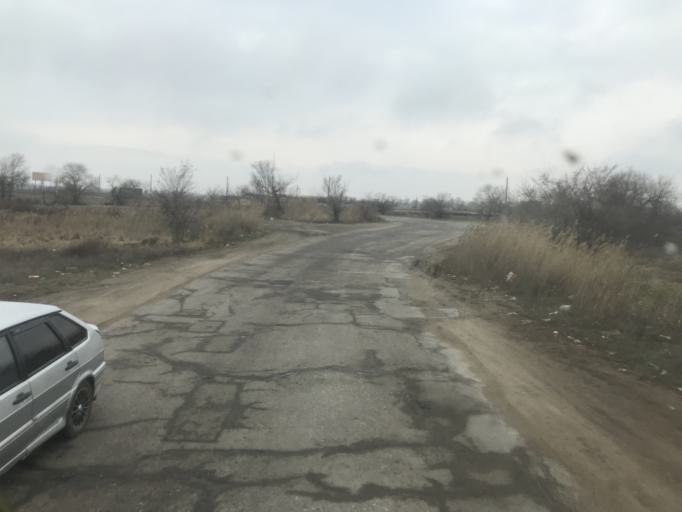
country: RU
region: Volgograd
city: Krasnoslobodsk
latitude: 48.5363
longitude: 44.6086
